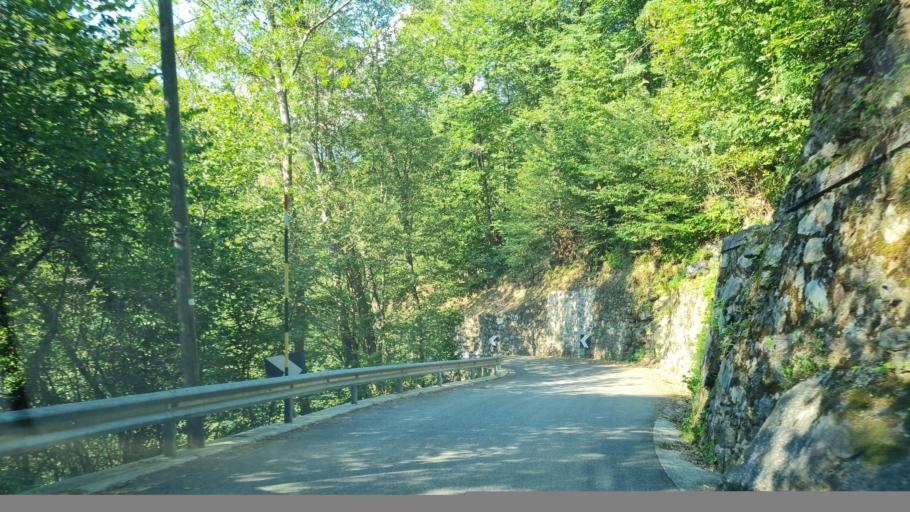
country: IT
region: Aosta Valley
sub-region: Valle d'Aosta
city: Lillianes
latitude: 45.6308
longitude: 7.8482
